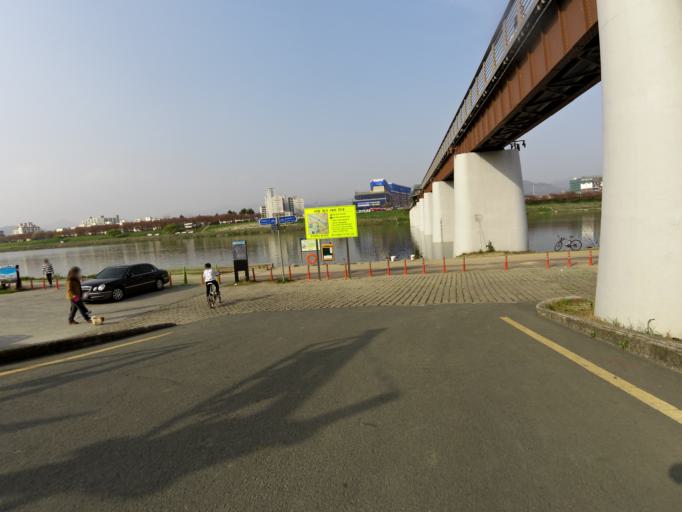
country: KR
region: Daegu
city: Daegu
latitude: 35.8893
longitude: 128.6375
